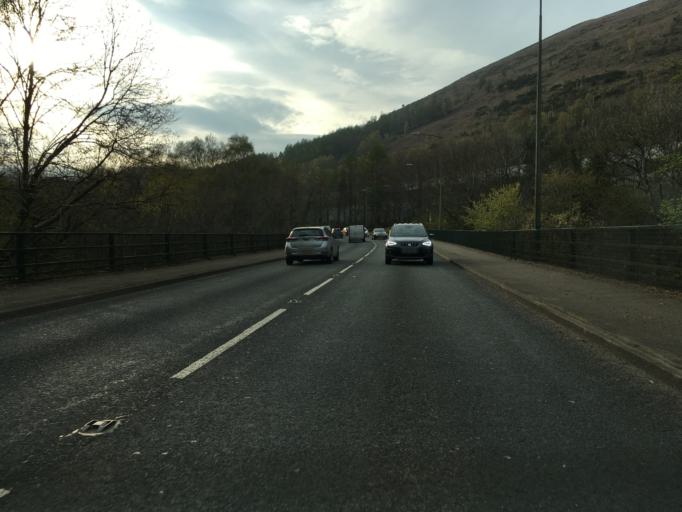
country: GB
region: Wales
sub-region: Caerphilly County Borough
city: Crosskeys
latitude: 51.6166
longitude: -3.1376
